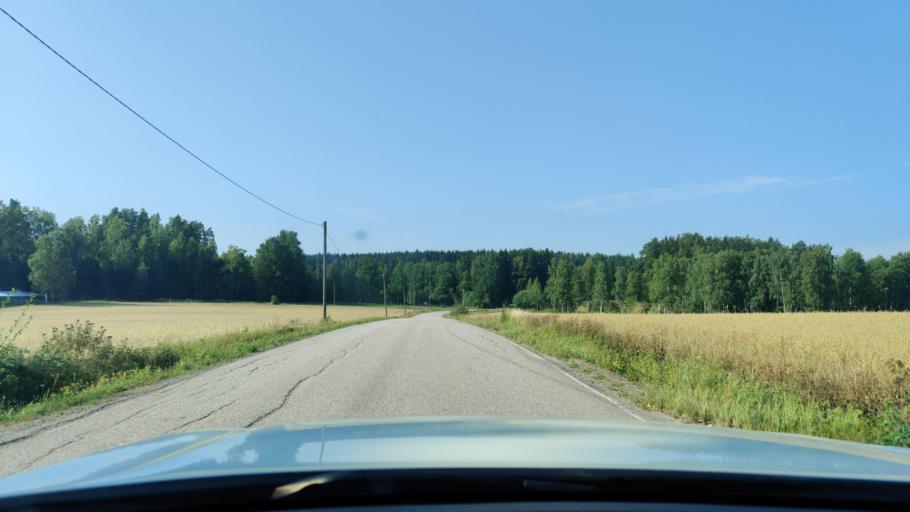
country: FI
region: Haeme
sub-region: Riihimaeki
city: Riihimaeki
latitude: 60.6890
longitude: 24.6737
